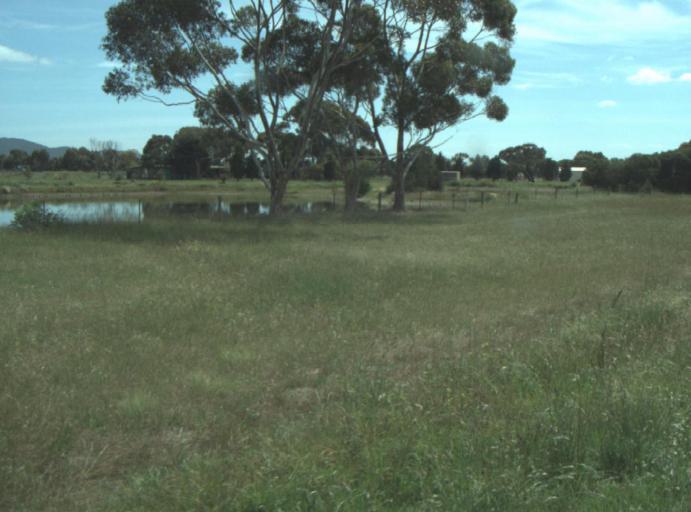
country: AU
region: Victoria
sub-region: Greater Geelong
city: Lara
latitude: -38.0190
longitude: 144.4450
